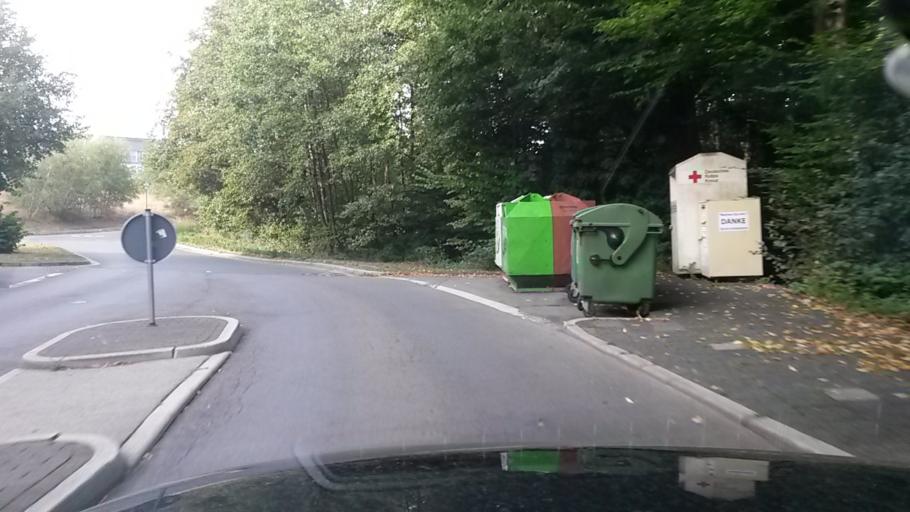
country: DE
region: North Rhine-Westphalia
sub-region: Regierungsbezirk Arnsberg
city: Luedenscheid
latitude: 51.2305
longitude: 7.6403
